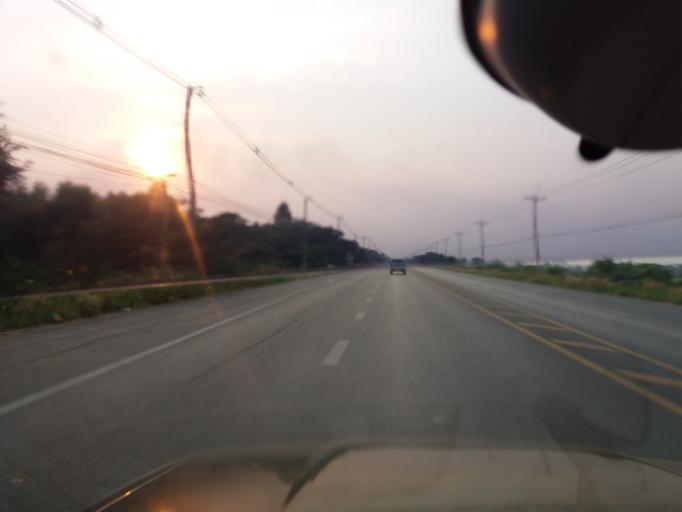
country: TH
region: Sing Buri
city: Bang Racham
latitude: 14.8829
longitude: 100.3425
